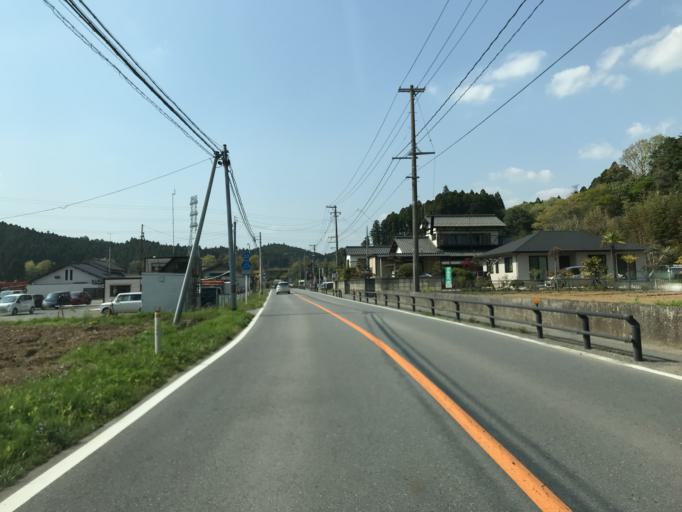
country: JP
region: Ibaraki
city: Kitaibaraki
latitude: 36.9327
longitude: 140.7736
